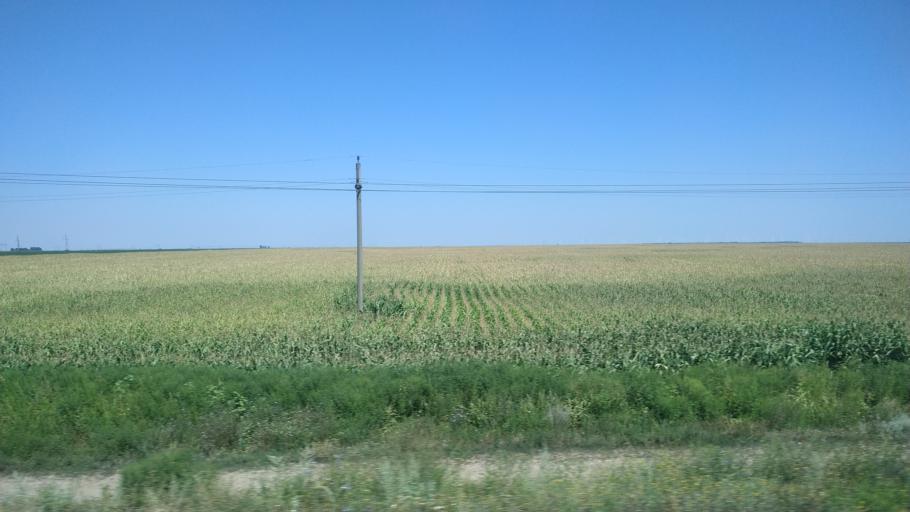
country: RO
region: Calarasi
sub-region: Comuna Borcea
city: Borcea
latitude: 44.4205
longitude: 27.6790
